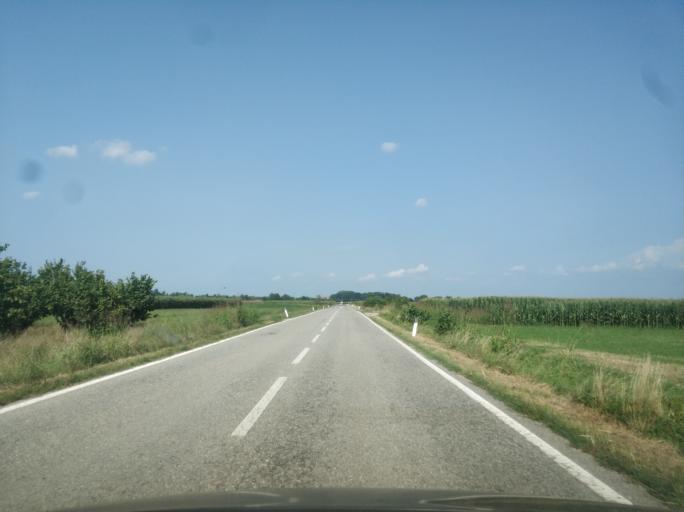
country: IT
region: Piedmont
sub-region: Provincia di Cuneo
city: Caraglio
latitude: 44.4375
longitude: 7.4480
